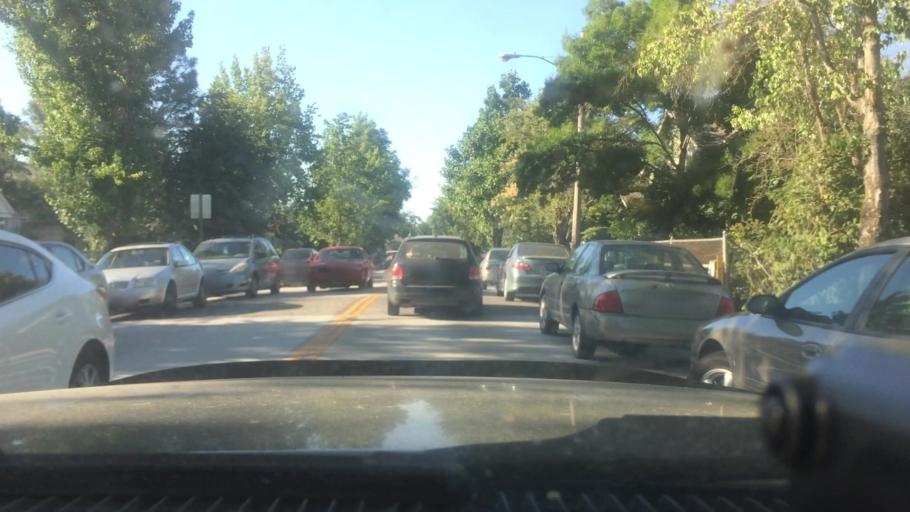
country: US
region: Oregon
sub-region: Lane County
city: Eugene
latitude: 44.0440
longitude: -123.1013
